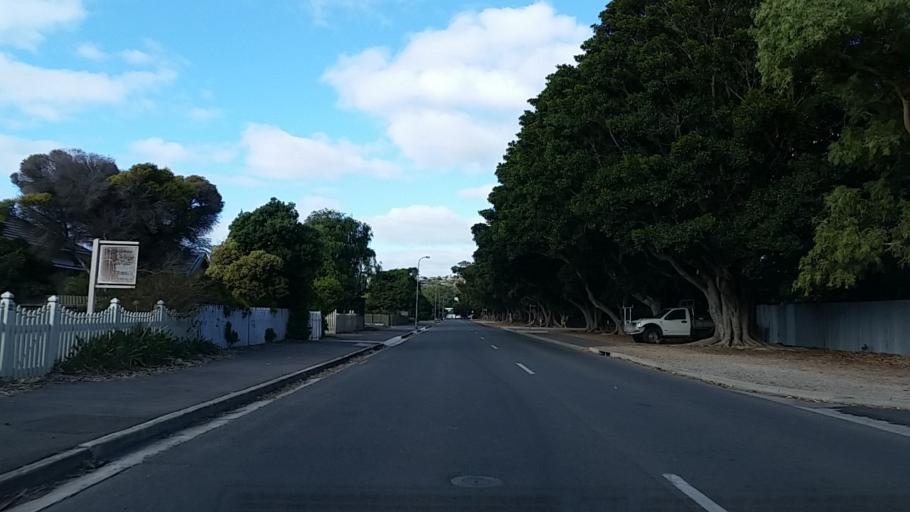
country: AU
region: South Australia
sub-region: Yankalilla
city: Normanville
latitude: -35.4453
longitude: 138.3131
